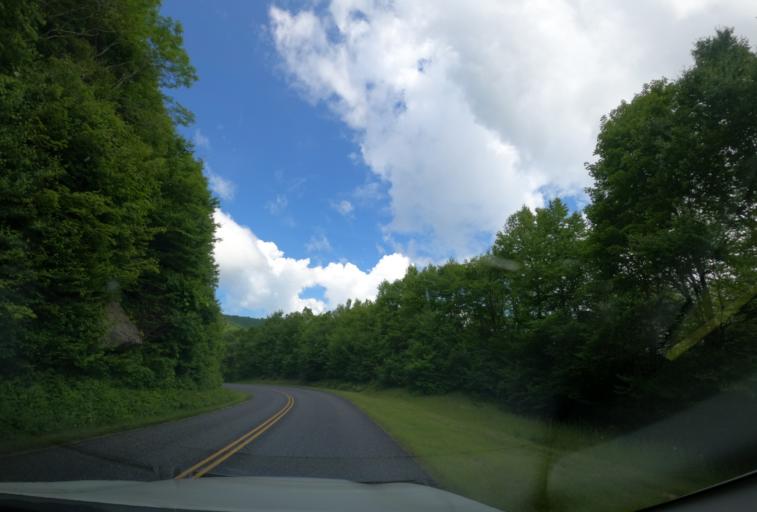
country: US
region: North Carolina
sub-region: Haywood County
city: Hazelwood
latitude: 35.4185
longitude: -83.0426
